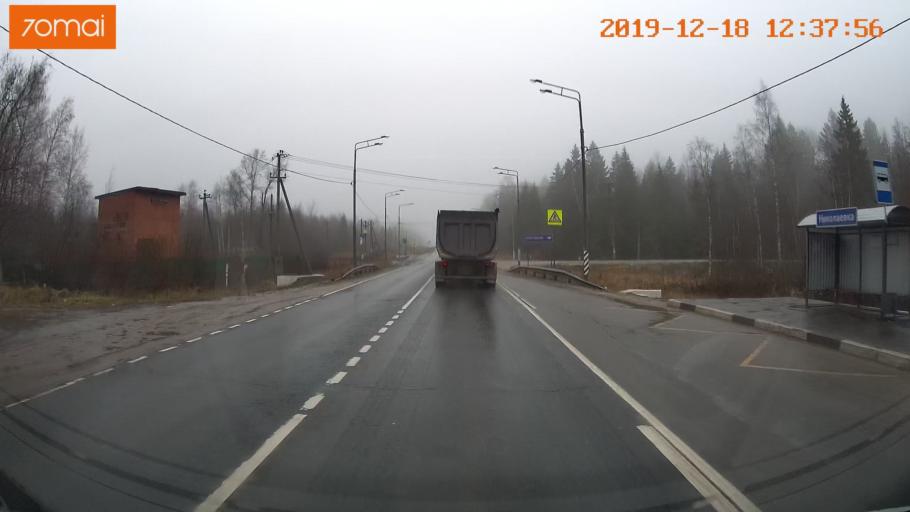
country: RU
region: Moskovskaya
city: Vysokovsk
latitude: 56.1472
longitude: 36.6027
